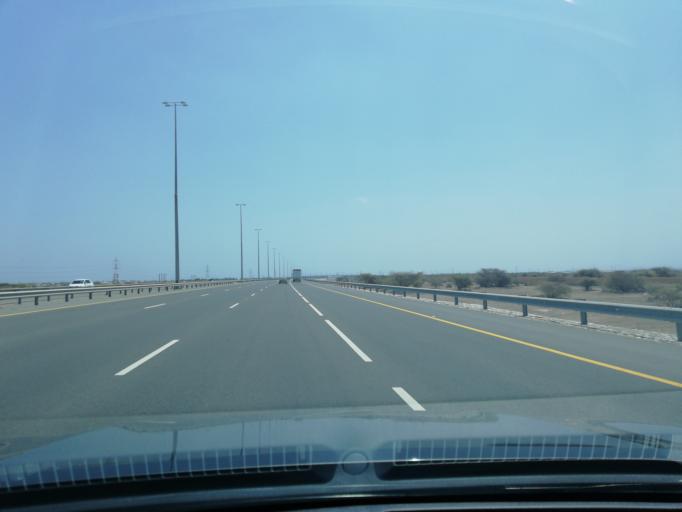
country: OM
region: Al Batinah
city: Barka'
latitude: 23.6303
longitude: 57.9680
